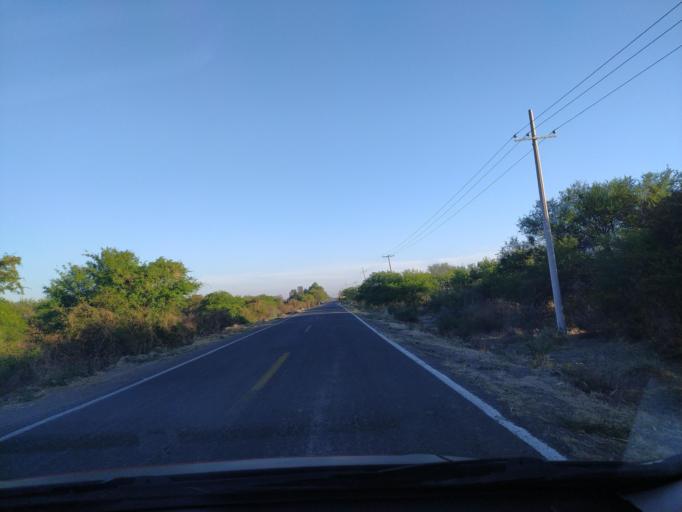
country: MX
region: Guanajuato
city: Ciudad Manuel Doblado
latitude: 20.7447
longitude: -101.8233
